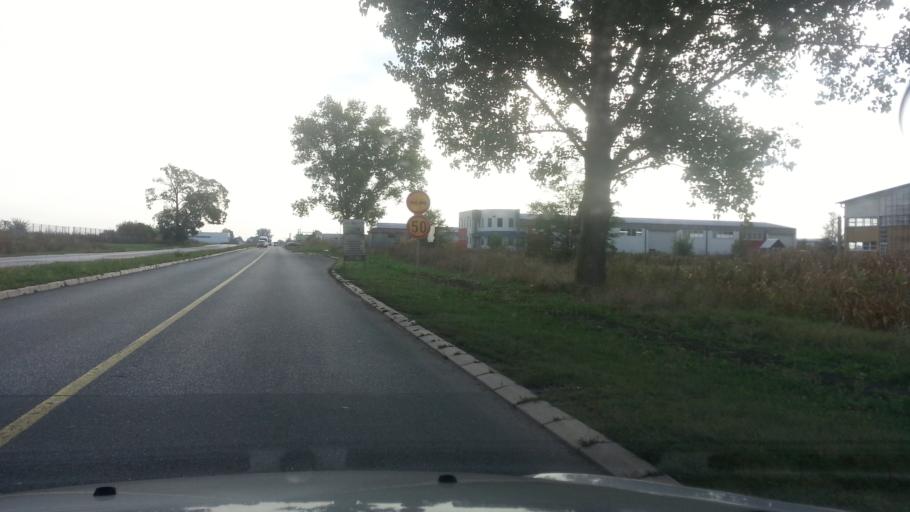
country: RS
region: Autonomna Pokrajina Vojvodina
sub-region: Sremski Okrug
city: Stara Pazova
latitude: 44.9867
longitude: 20.1923
